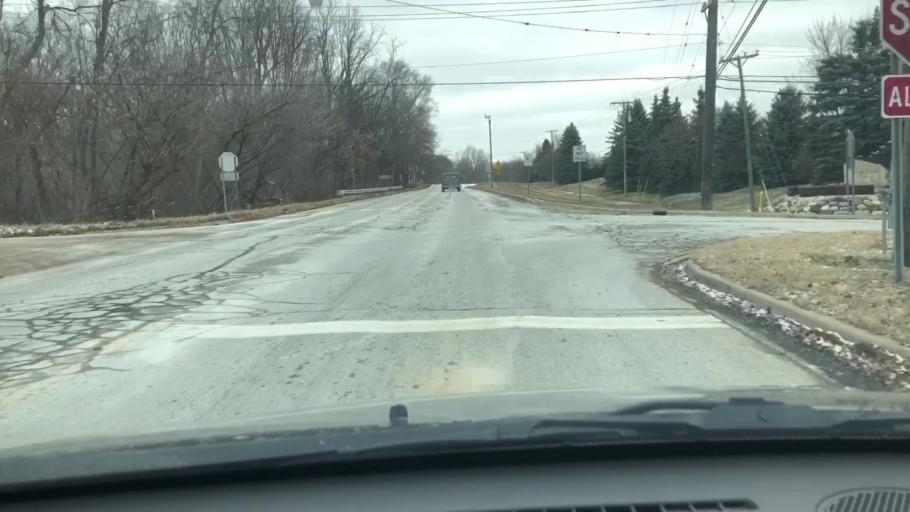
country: US
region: Michigan
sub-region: Macomb County
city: Shelby
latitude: 42.7231
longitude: -83.0562
